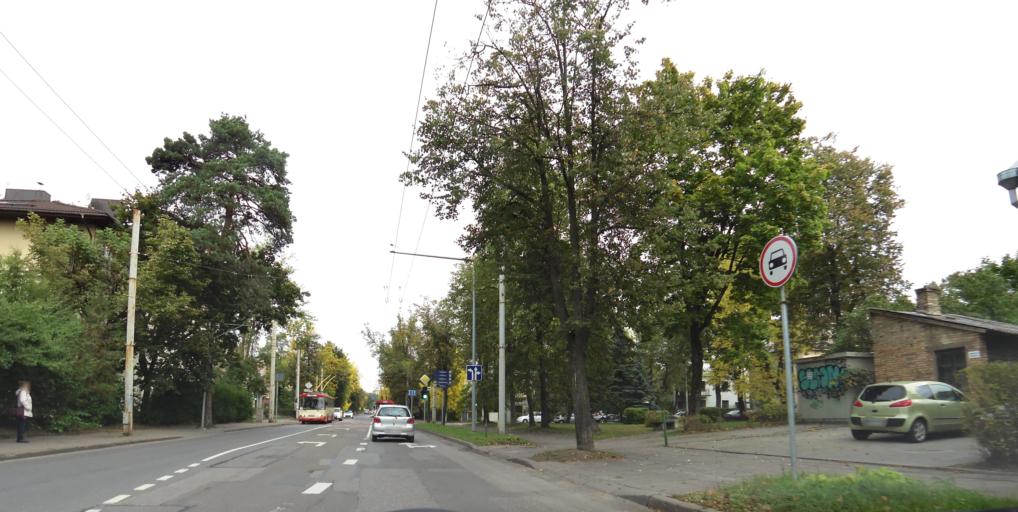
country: LT
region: Vilnius County
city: Naujamiestis
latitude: 54.6895
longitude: 25.2520
